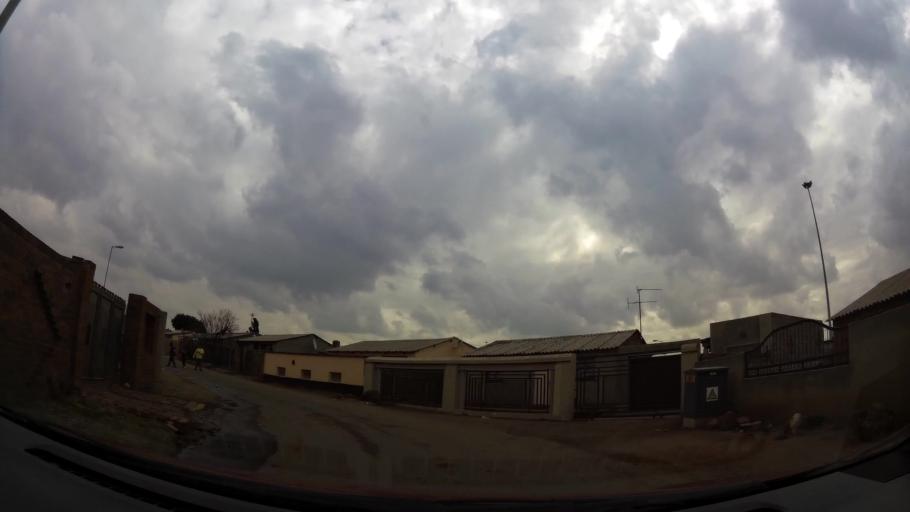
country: ZA
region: Gauteng
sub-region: City of Johannesburg Metropolitan Municipality
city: Soweto
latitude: -26.2605
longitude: 27.8368
